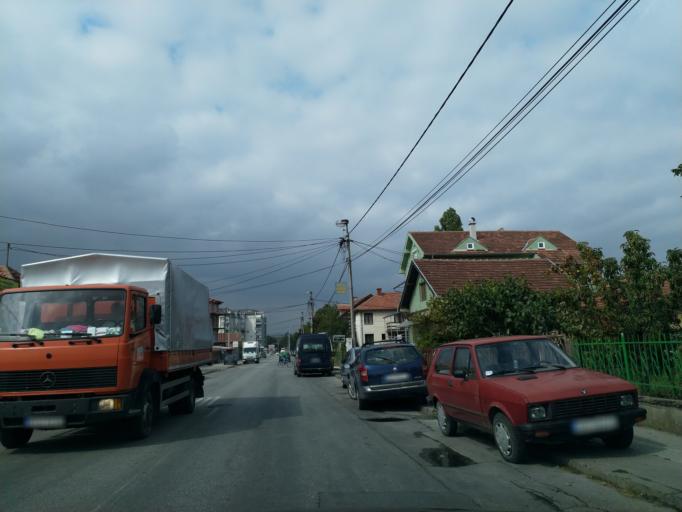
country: RS
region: Central Serbia
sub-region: Pomoravski Okrug
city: Jagodina
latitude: 43.9851
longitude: 21.2531
